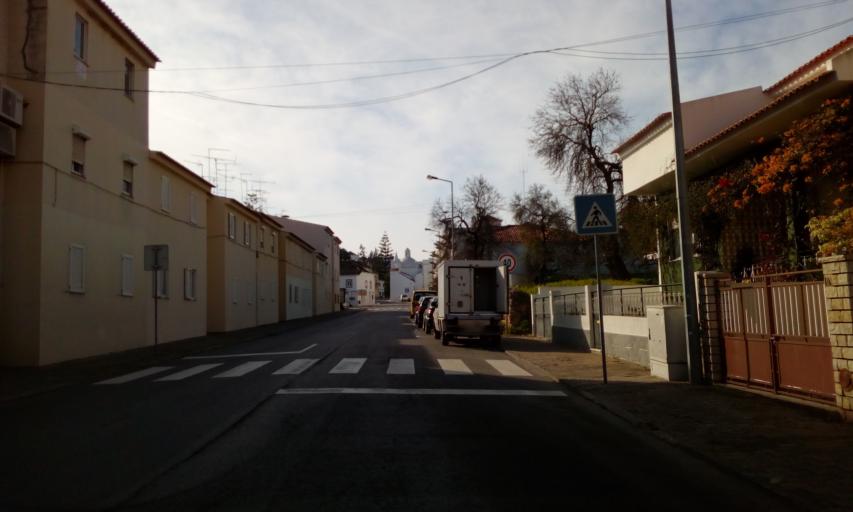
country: PT
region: Faro
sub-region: Tavira
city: Tavira
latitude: 37.1271
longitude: -7.6532
